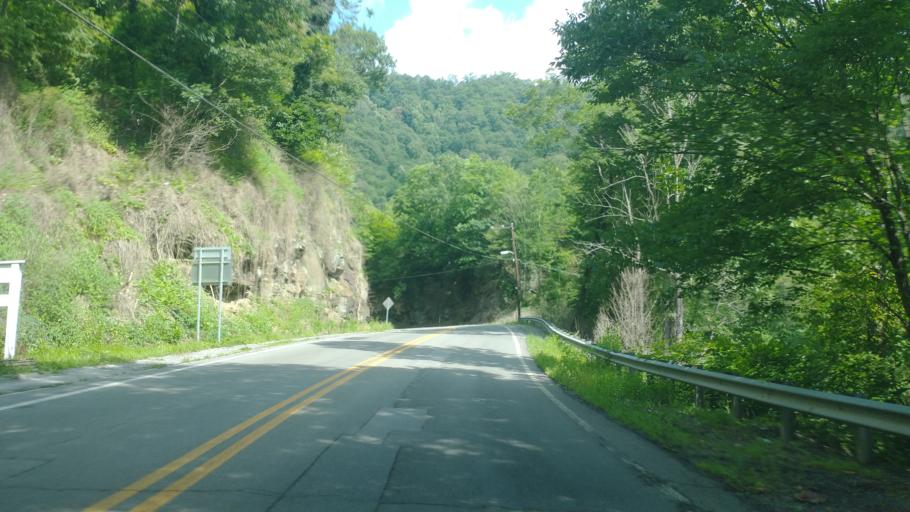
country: US
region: West Virginia
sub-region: McDowell County
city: Welch
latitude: 37.4200
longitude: -81.4405
